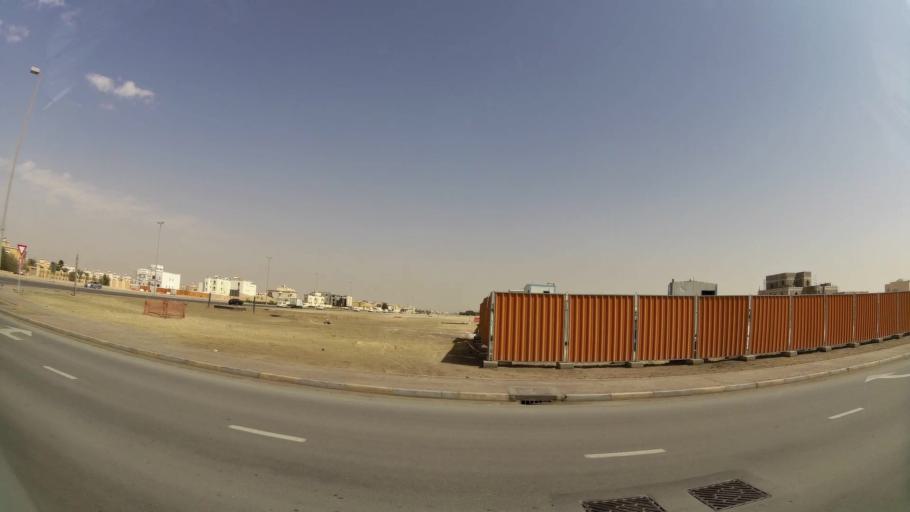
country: AE
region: Abu Dhabi
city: Abu Dhabi
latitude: 24.3242
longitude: 54.5393
